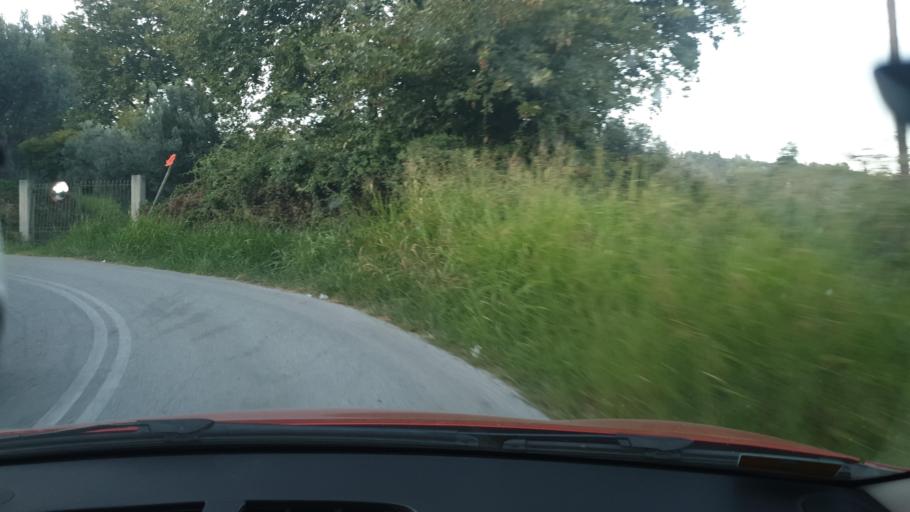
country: GR
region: Central Greece
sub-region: Nomos Evvoias
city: Kymi
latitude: 38.6321
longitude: 24.1240
